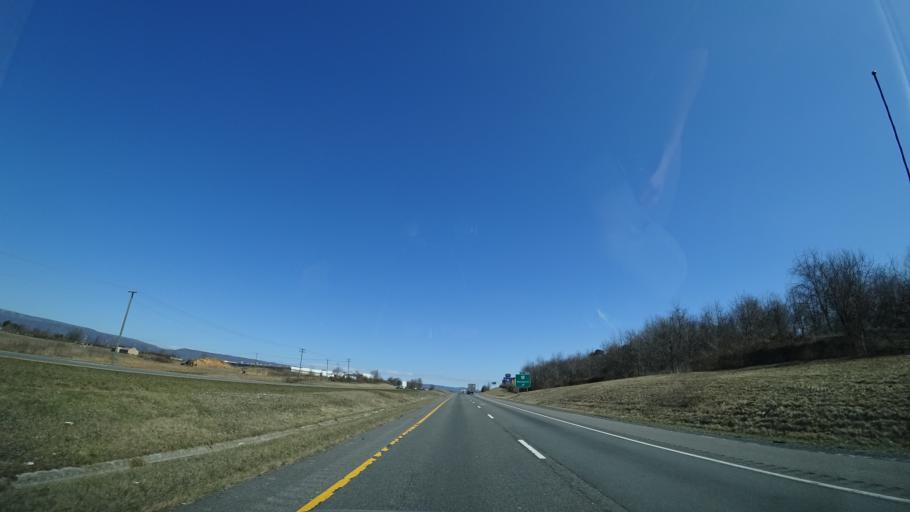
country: US
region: Virginia
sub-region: Shenandoah County
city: Woodstock
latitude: 38.8648
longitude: -78.5311
